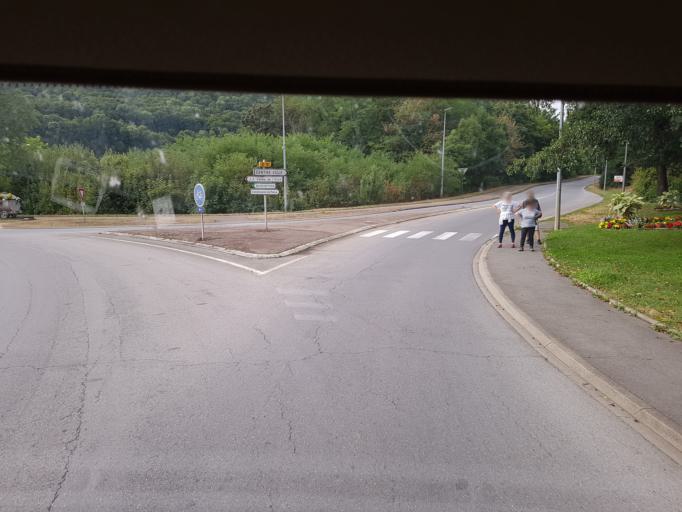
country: FR
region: Lorraine
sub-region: Departement de la Moselle
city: Moyeuvre-Grande
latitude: 49.2512
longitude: 6.0540
